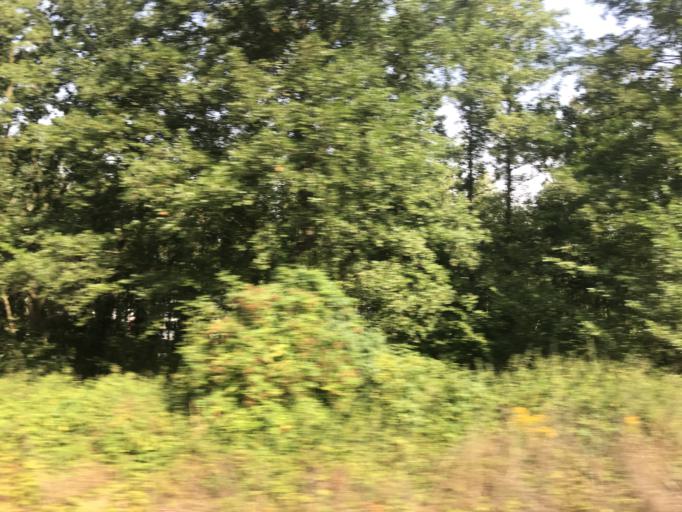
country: CZ
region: Central Bohemia
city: Bystrice
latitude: 49.7433
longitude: 14.6701
